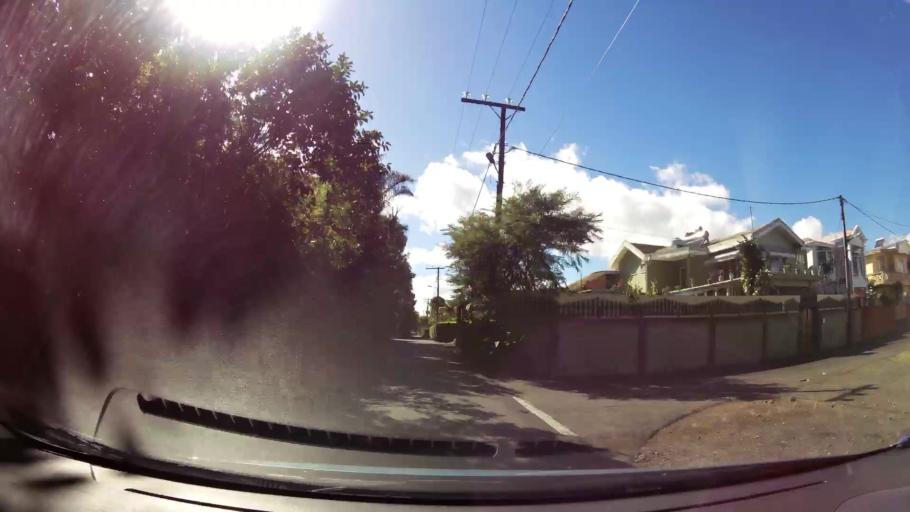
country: MU
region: Plaines Wilhems
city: Vacoas
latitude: -20.3013
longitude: 57.4957
